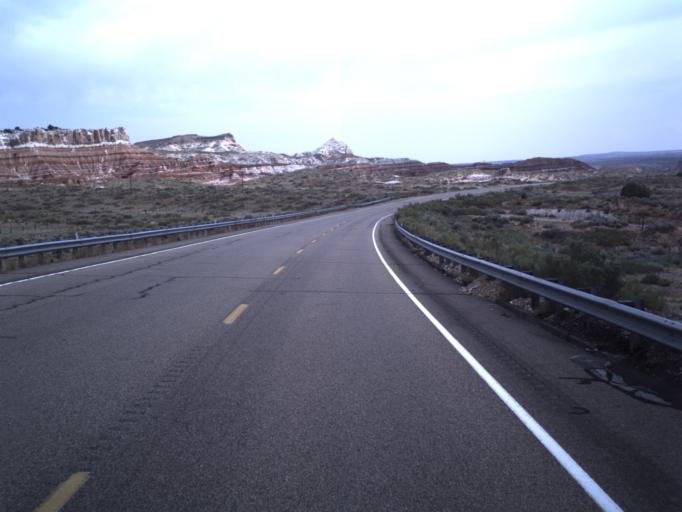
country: US
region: Arizona
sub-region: Coconino County
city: Page
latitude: 37.1277
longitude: -111.9550
